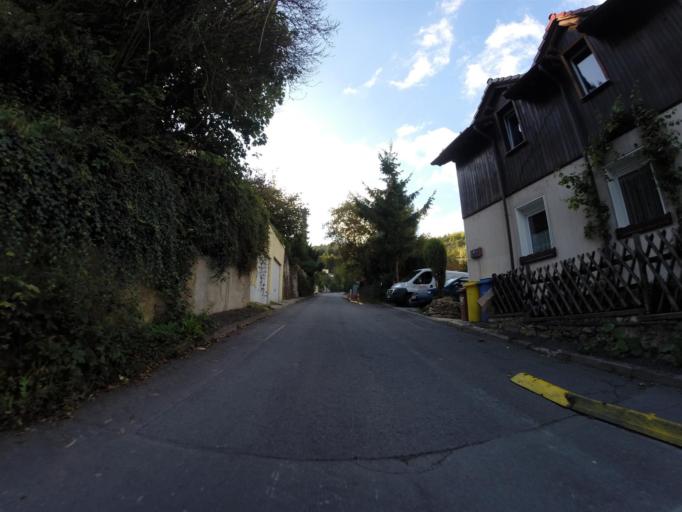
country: DE
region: Thuringia
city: Jena
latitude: 50.9371
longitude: 11.5846
